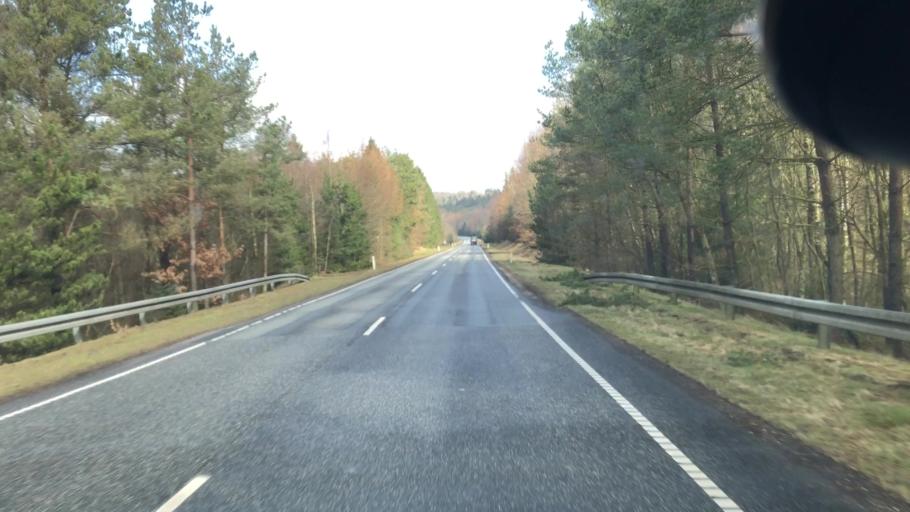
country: DK
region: Central Jutland
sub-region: Silkeborg Kommune
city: Virklund
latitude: 56.0630
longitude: 9.5803
